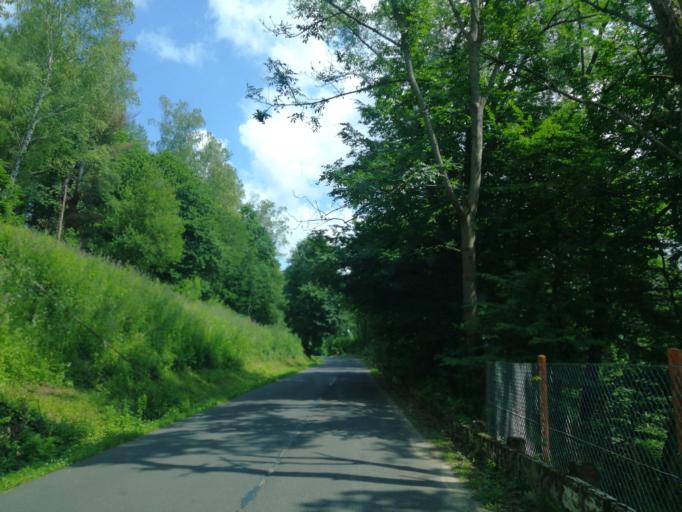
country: PL
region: Subcarpathian Voivodeship
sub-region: Powiat leski
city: Uherce Mineralne
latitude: 49.4300
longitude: 22.4139
